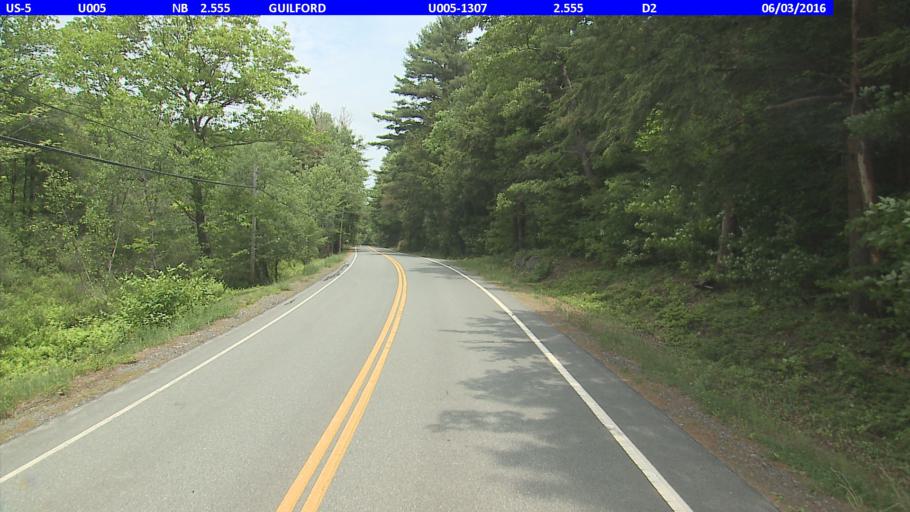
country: US
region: New Hampshire
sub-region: Cheshire County
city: Hinsdale
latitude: 42.7662
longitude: -72.5678
